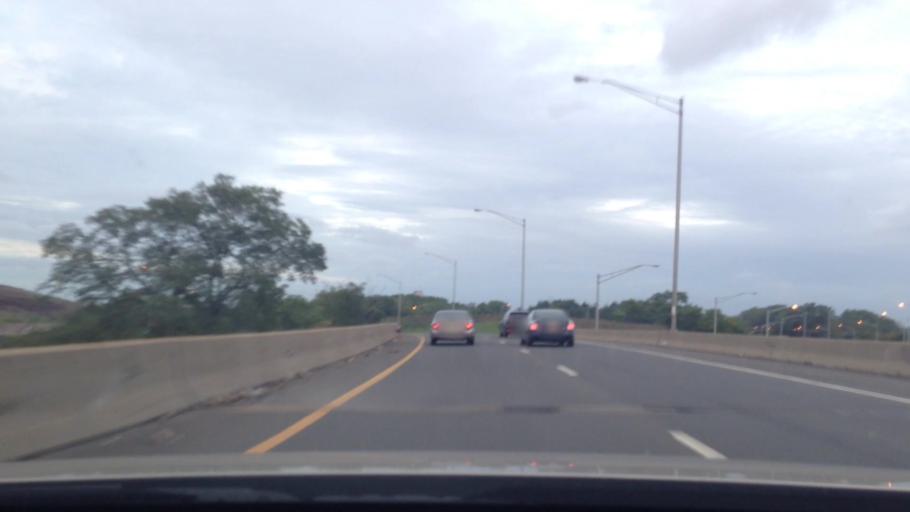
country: US
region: New Jersey
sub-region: Hudson County
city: Kearny
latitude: 40.7504
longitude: -74.1238
